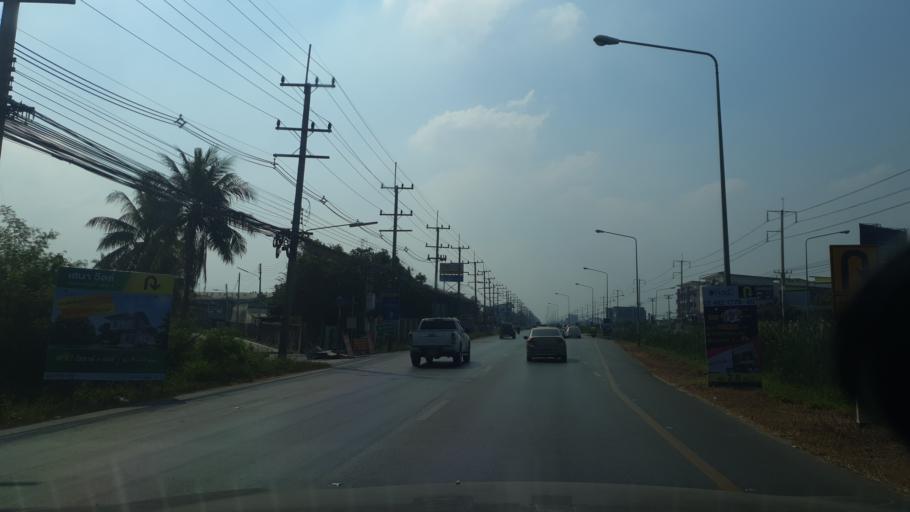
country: TH
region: Nakhon Pathom
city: Salaya
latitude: 13.7734
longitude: 100.3020
